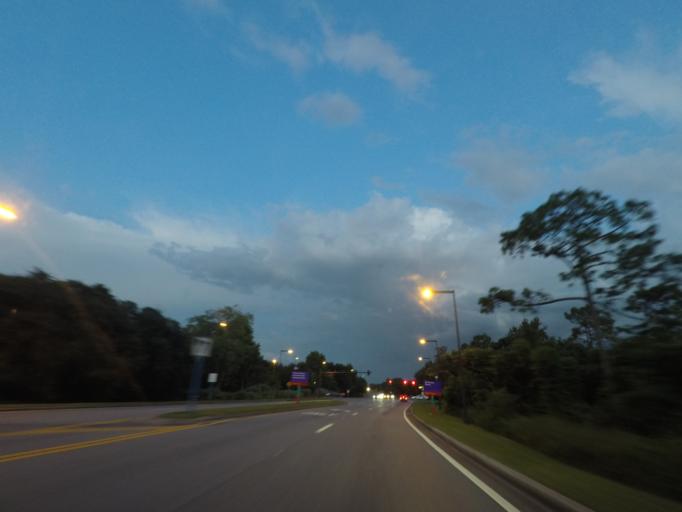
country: US
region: Florida
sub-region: Polk County
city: Citrus Ridge
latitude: 28.3512
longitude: -81.5979
